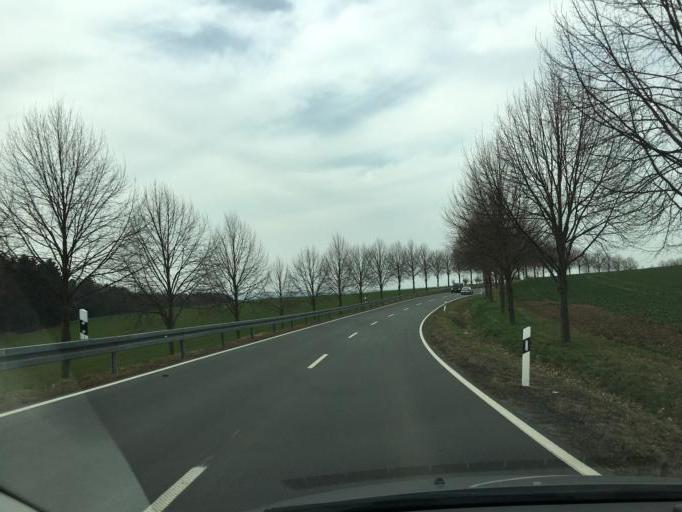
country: DE
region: Saxony
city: Hohenstein-Ernstthal
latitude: 50.8248
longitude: 12.7044
